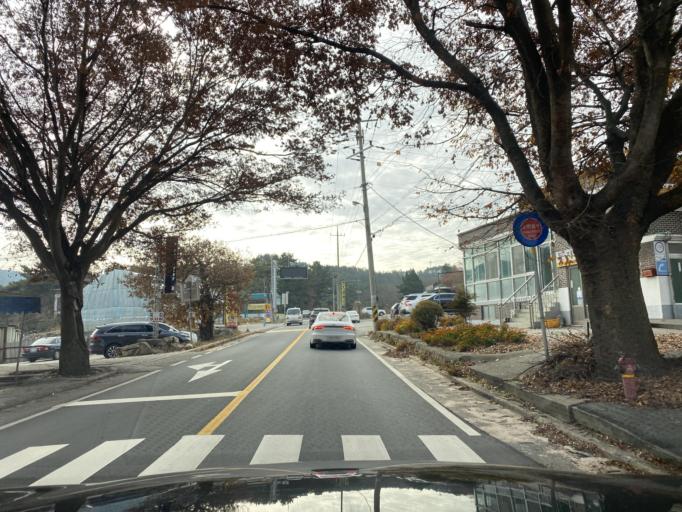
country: KR
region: Chungcheongnam-do
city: Hongsung
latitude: 36.6746
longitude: 126.6425
